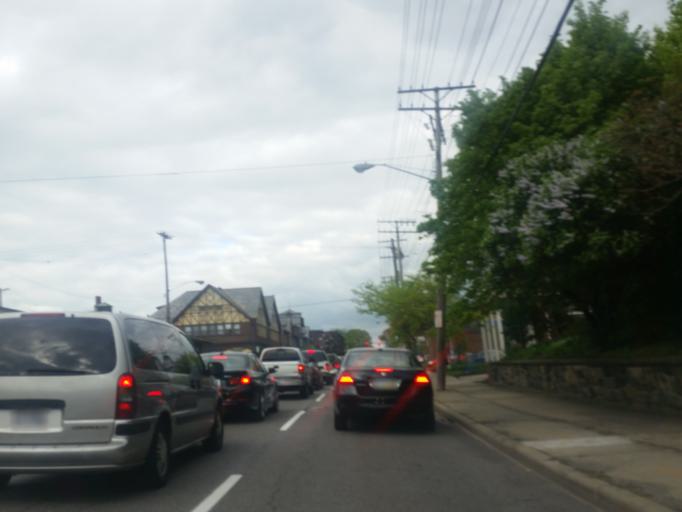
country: US
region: Ohio
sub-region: Cuyahoga County
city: East Cleveland
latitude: 41.5010
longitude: -81.5955
